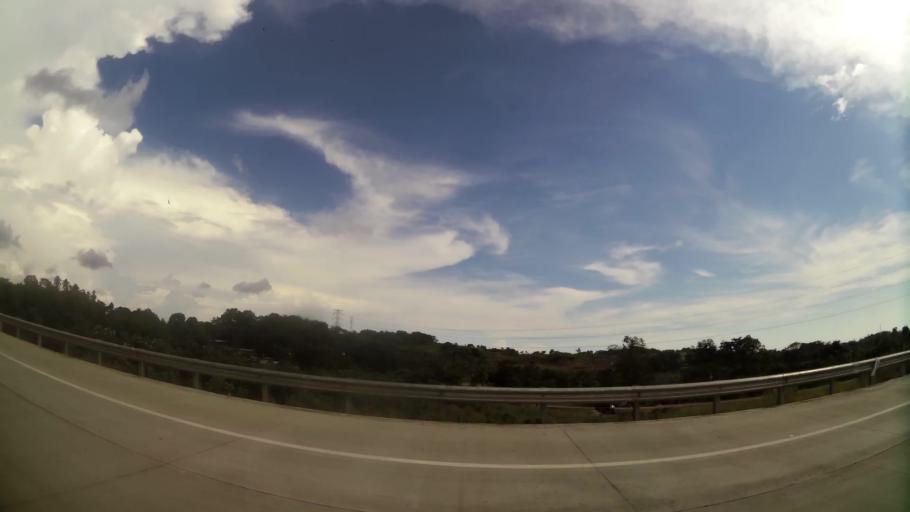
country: PA
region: Panama
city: Tocumen
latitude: 9.0930
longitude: -79.4236
